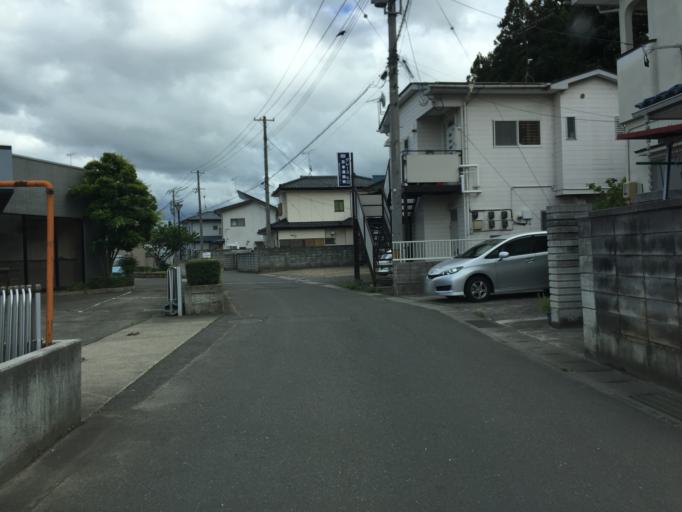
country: JP
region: Fukushima
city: Fukushima-shi
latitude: 37.7779
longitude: 140.4822
